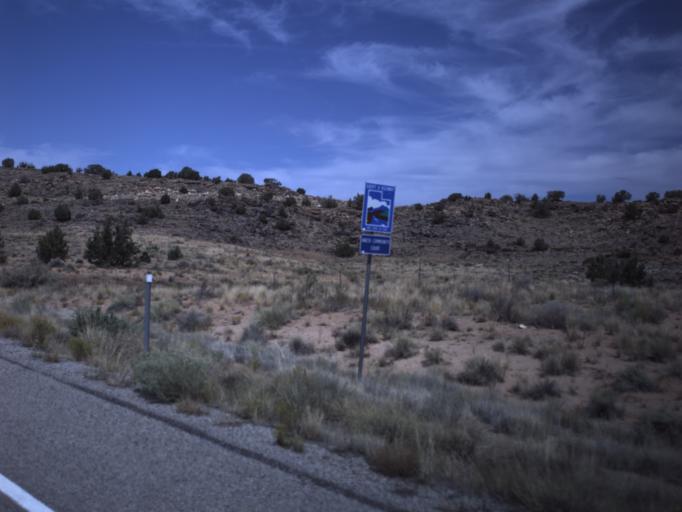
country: US
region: Colorado
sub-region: Montezuma County
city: Towaoc
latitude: 37.1917
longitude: -109.1290
